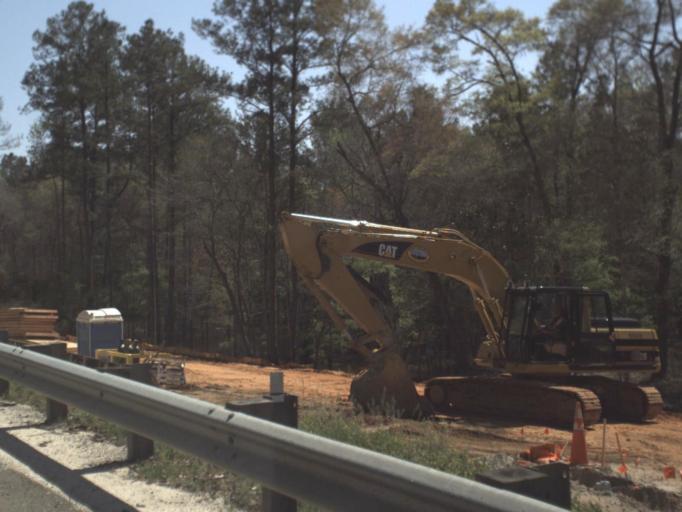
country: US
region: Florida
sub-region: Calhoun County
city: Blountstown
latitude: 30.4307
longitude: -85.1713
